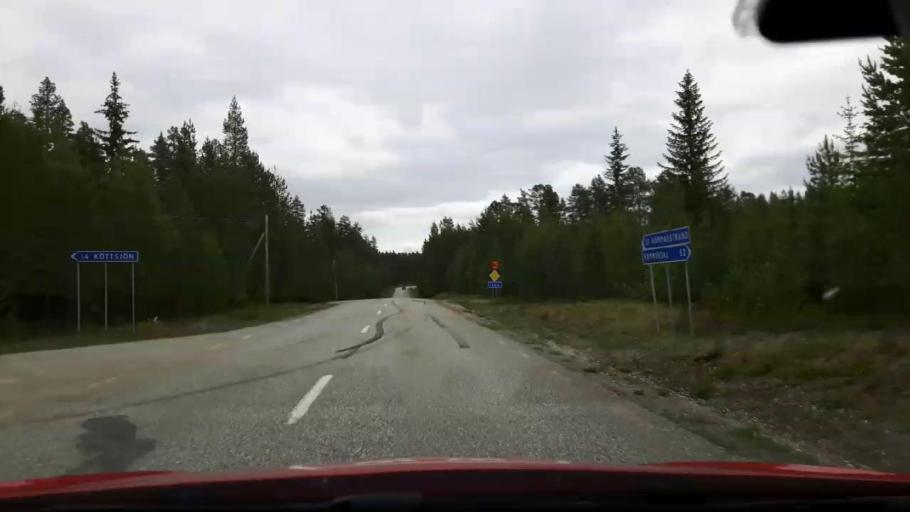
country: SE
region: Jaemtland
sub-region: Ragunda Kommun
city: Hammarstrand
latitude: 63.2529
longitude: 15.9043
